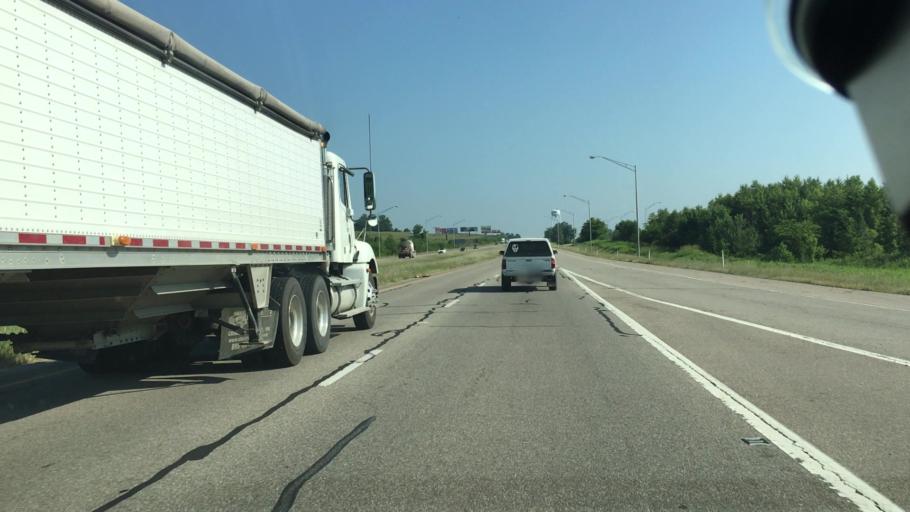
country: US
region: Indiana
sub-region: Gibson County
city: Fort Branch
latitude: 38.2775
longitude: -87.5675
